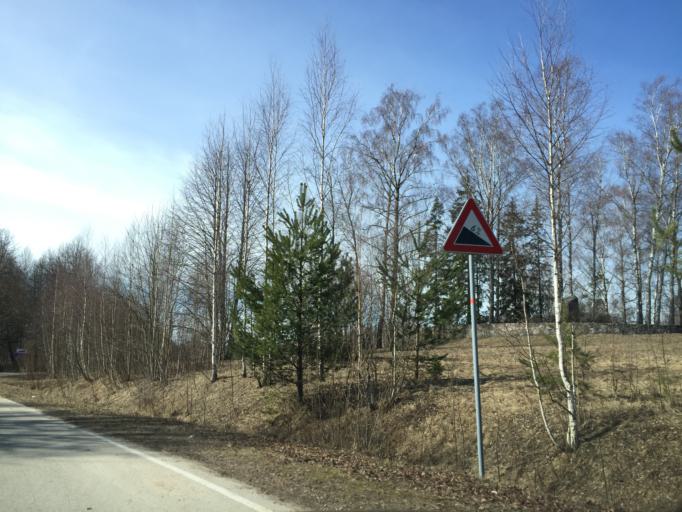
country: LV
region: Sigulda
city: Sigulda
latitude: 57.1384
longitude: 24.8219
